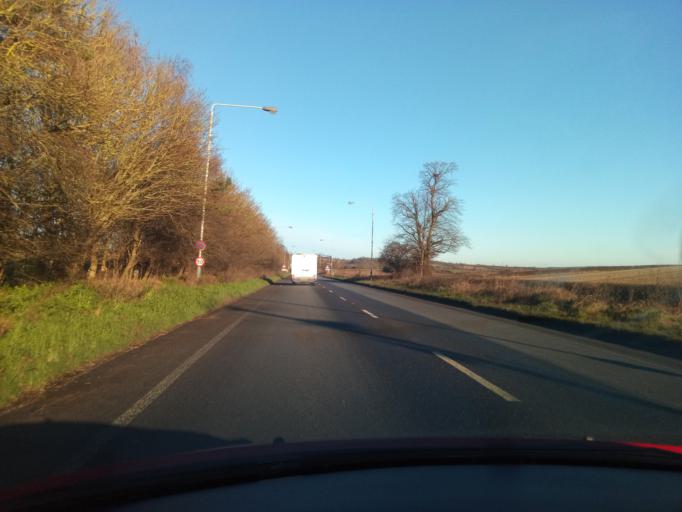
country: GB
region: England
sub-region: Nottinghamshire
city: Farnsfield
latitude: 53.1010
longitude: -1.0649
